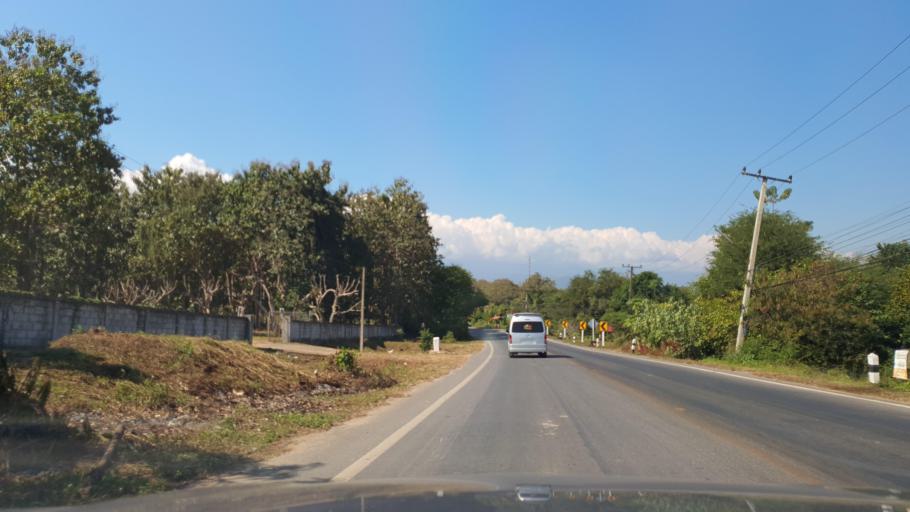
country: TH
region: Nan
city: Tha Wang Pha
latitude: 19.1045
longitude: 100.8190
